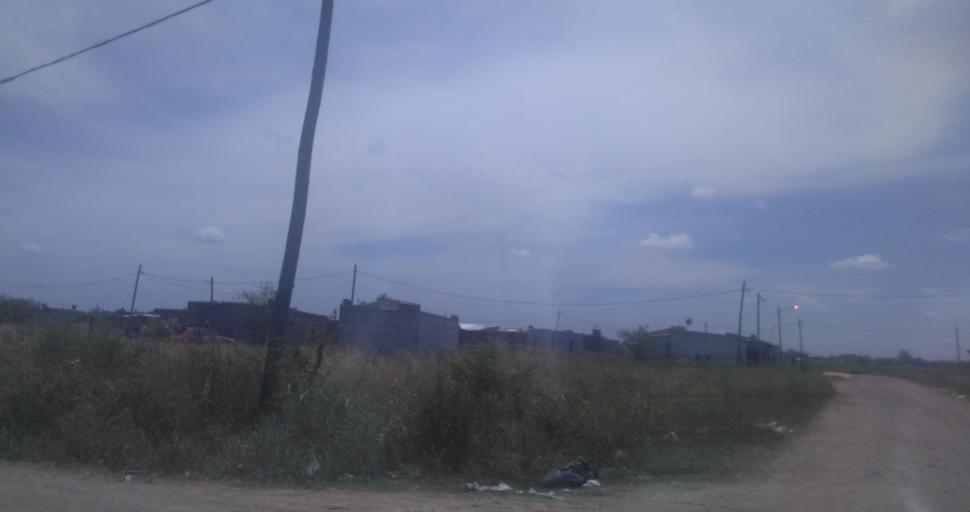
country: AR
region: Chaco
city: Fontana
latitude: -27.4237
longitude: -59.0418
